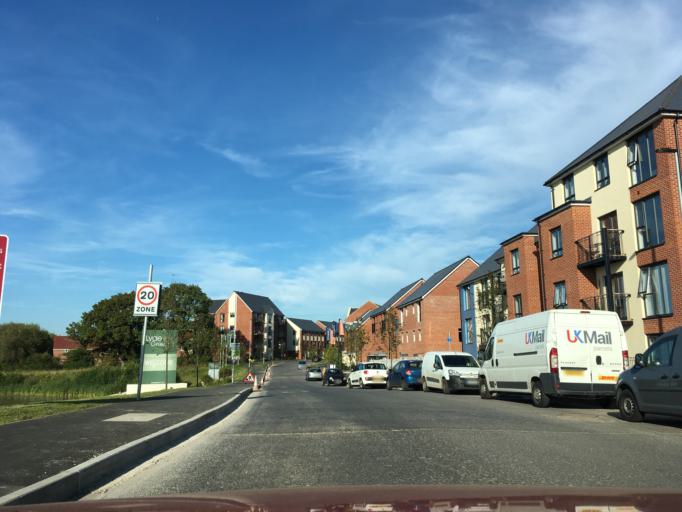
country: GB
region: England
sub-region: South Gloucestershire
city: Mangotsfield
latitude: 51.5015
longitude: -2.4751
